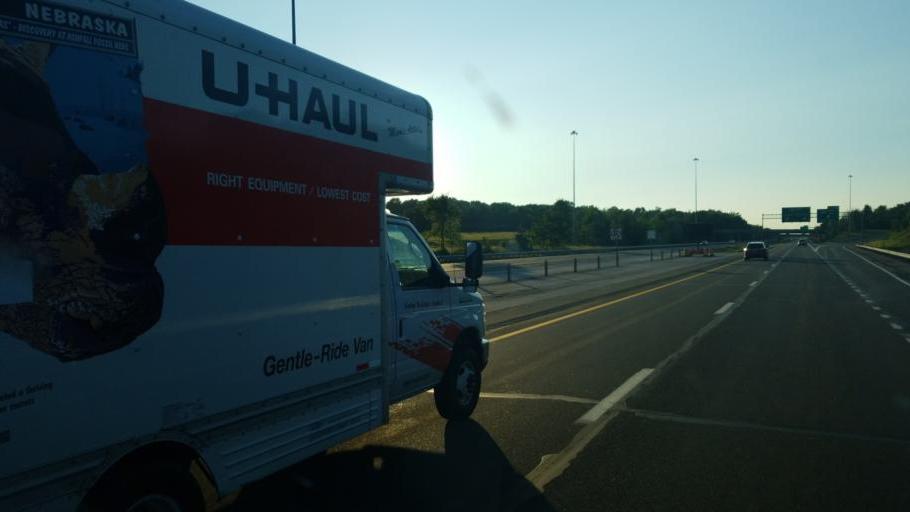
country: US
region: Ohio
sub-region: Mahoning County
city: Poland
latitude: 40.9528
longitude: -80.6355
